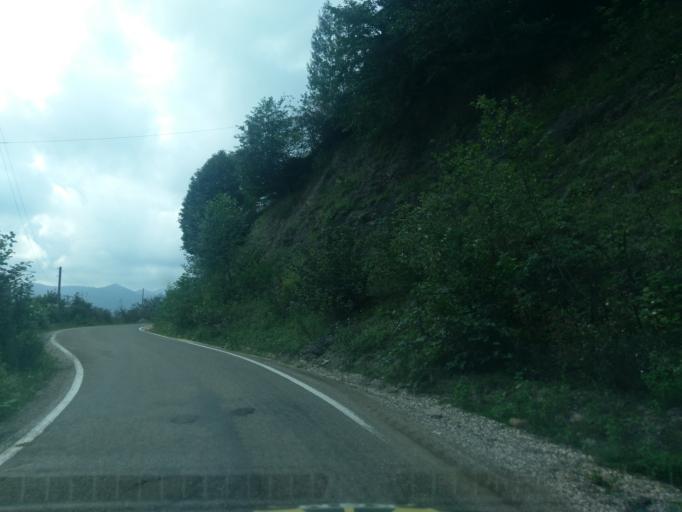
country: TR
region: Ordu
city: Gurgentepe
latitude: 40.8698
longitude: 37.6367
